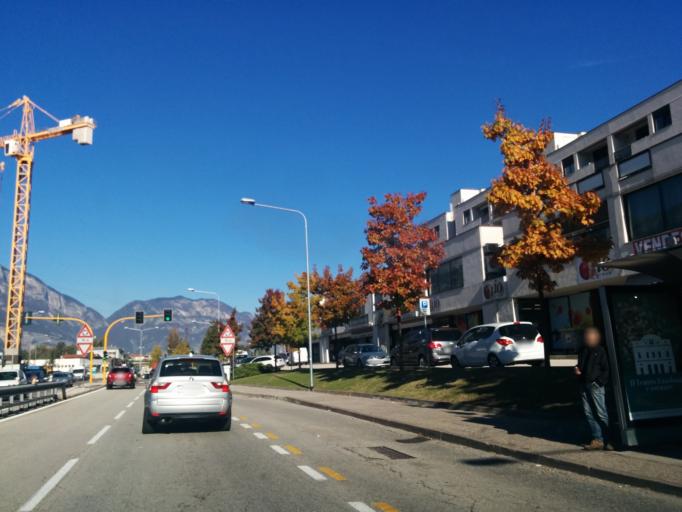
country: IT
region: Trentino-Alto Adige
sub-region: Provincia di Trento
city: Trento
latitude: 46.0913
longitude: 11.1156
